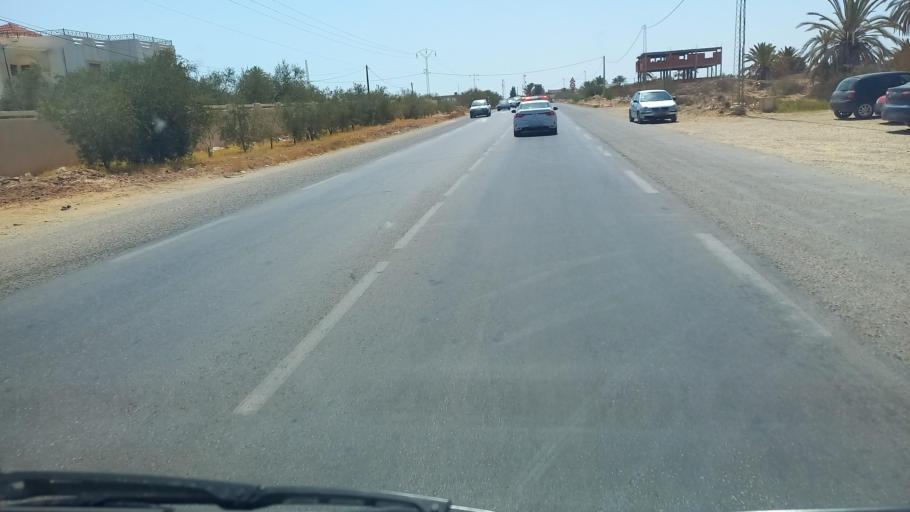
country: TN
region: Madanin
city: Houmt Souk
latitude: 33.8128
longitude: 10.8769
